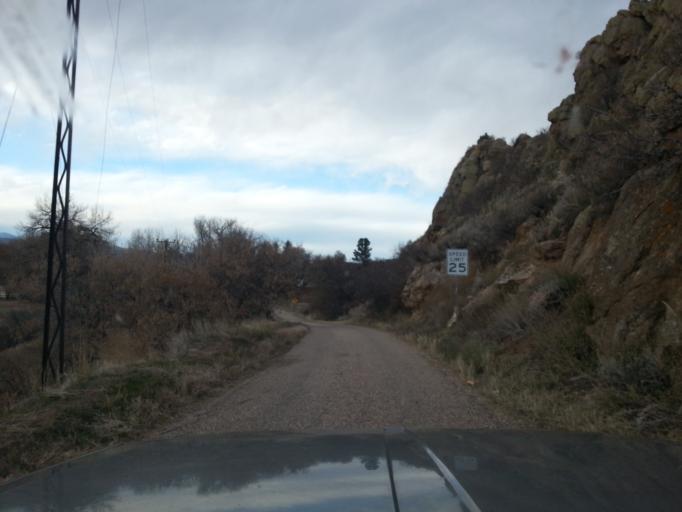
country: US
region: Colorado
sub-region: Larimer County
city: Loveland
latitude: 40.4084
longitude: -105.1527
